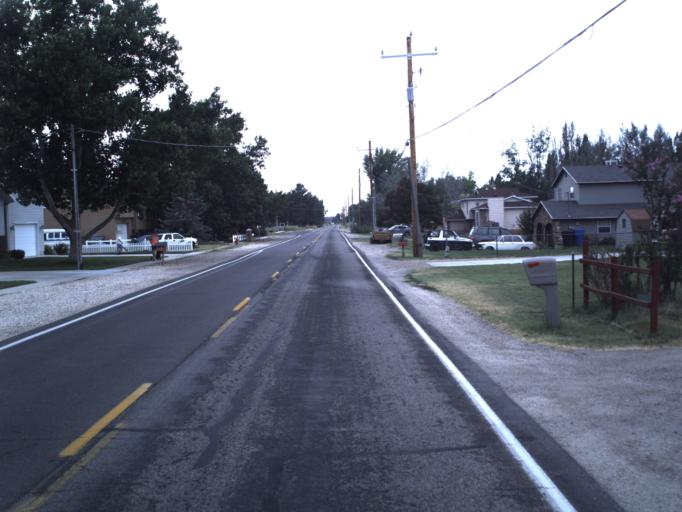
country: US
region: Utah
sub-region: Davis County
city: West Point
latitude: 41.1158
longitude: -112.1126
